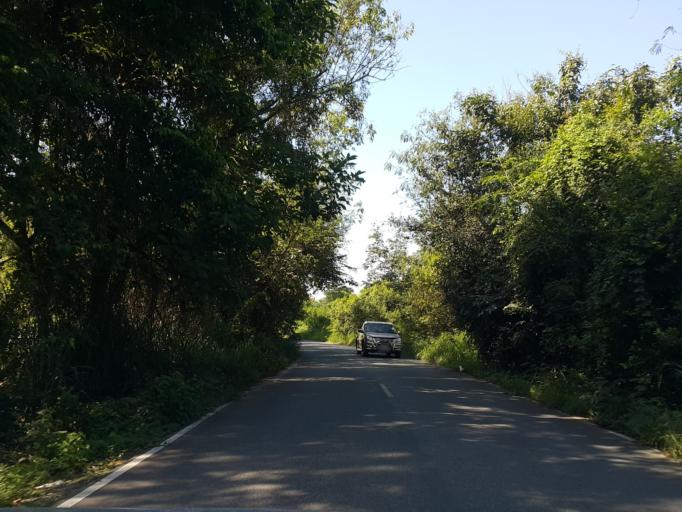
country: TH
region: Chiang Mai
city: Mae On
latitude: 18.8136
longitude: 99.1757
